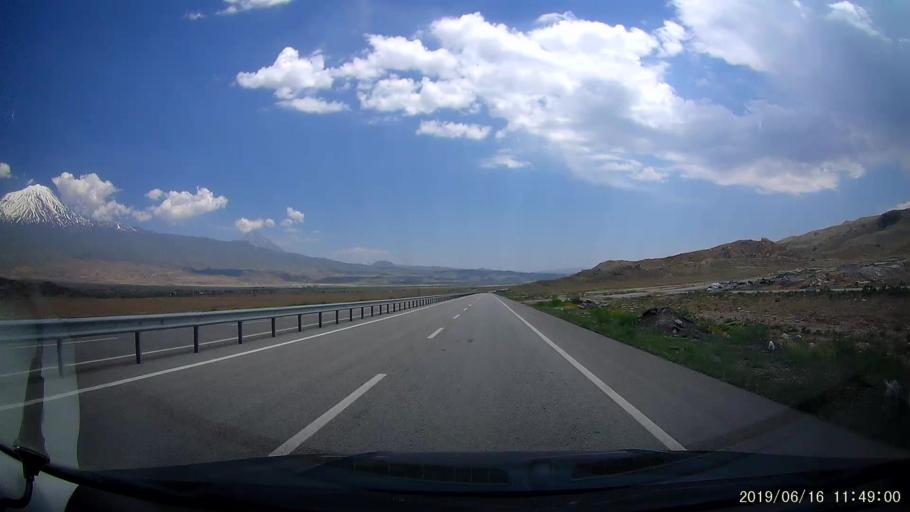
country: TR
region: Agri
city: Dogubayazit
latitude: 39.5577
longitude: 44.1549
